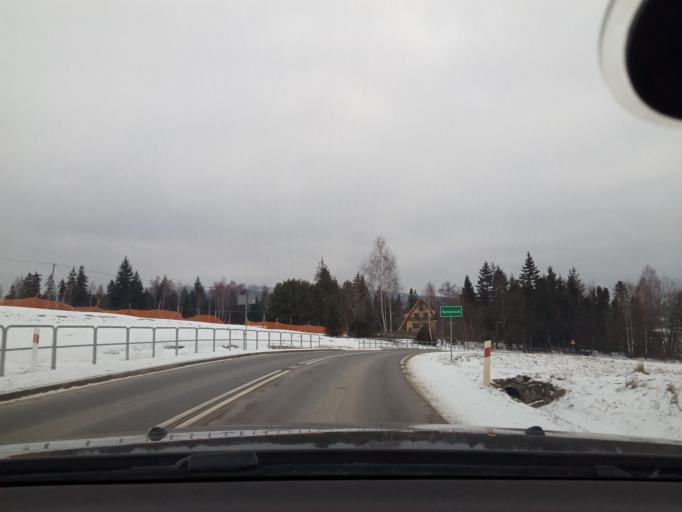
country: PL
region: Lesser Poland Voivodeship
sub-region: Powiat nowotarski
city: Krosnica
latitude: 49.4402
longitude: 20.3368
